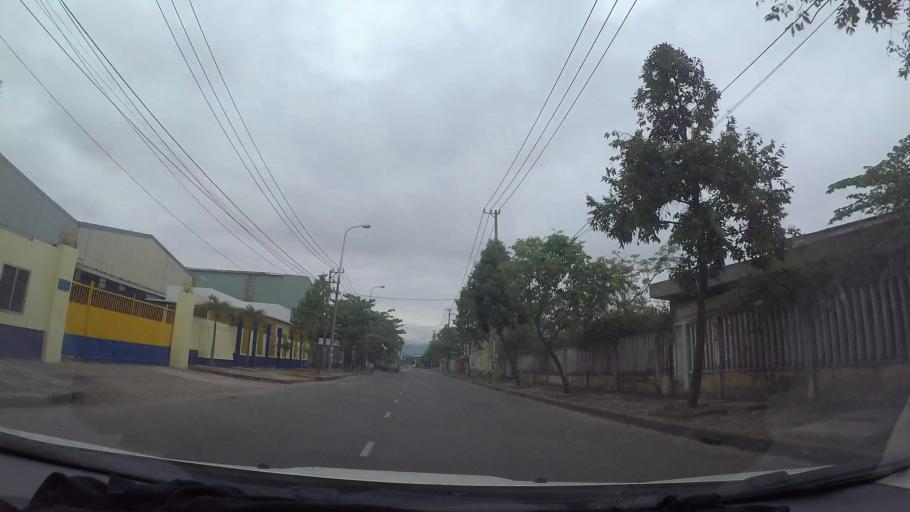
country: VN
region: Da Nang
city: Lien Chieu
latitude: 16.0850
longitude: 108.1389
